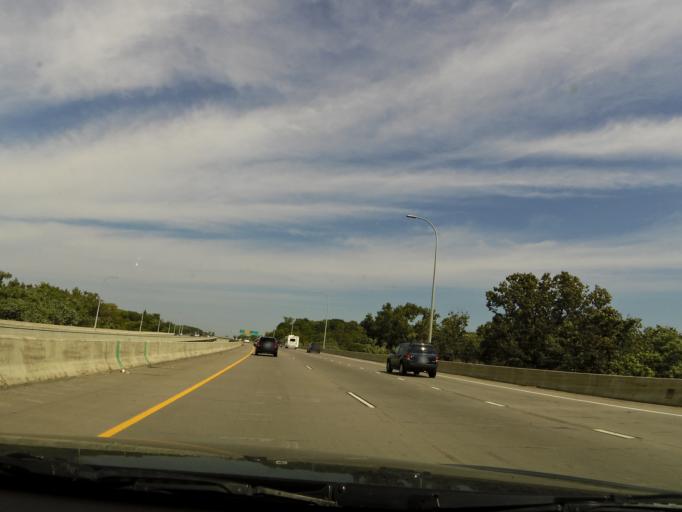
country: US
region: Minnesota
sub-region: Scott County
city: Savage
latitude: 44.8009
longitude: -93.3983
